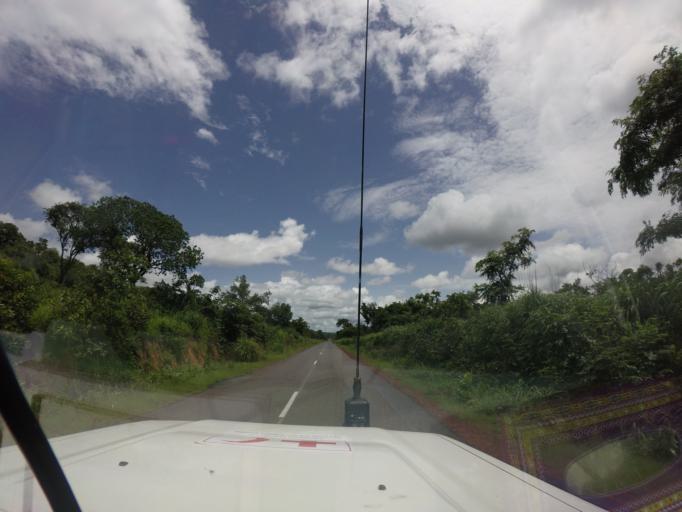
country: SL
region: Northern Province
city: Gberia Fotombu
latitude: 10.0610
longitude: -11.0546
